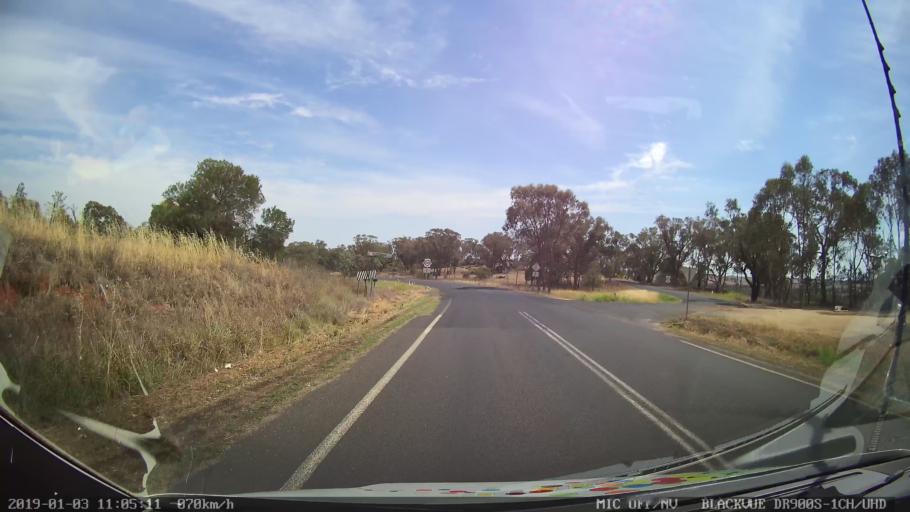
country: AU
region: New South Wales
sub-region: Young
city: Young
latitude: -34.2744
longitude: 148.2862
